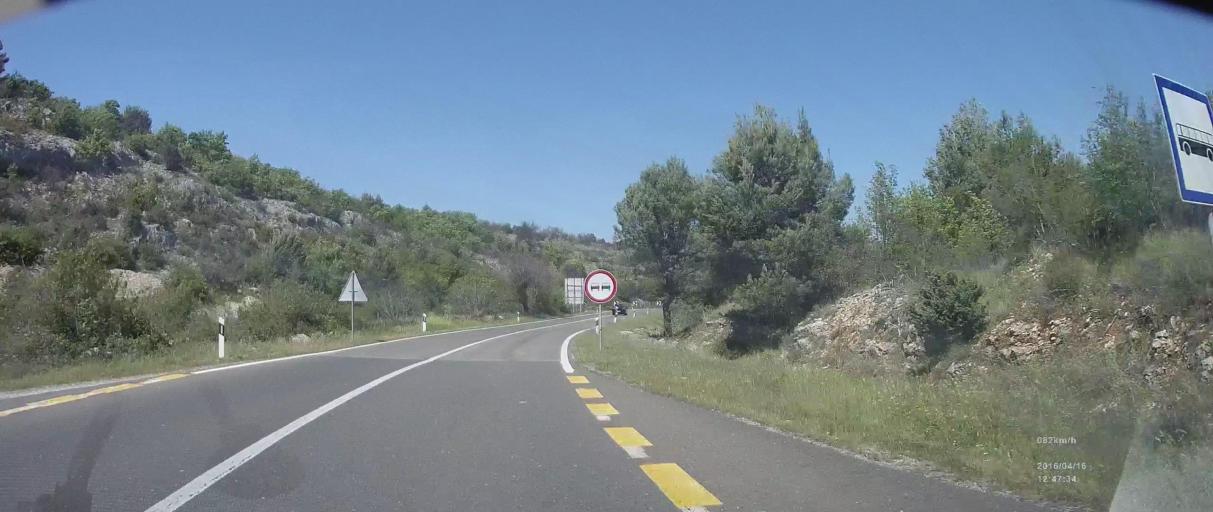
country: HR
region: Sibensko-Kniniska
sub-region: Grad Sibenik
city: Brodarica
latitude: 43.6653
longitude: 16.0453
